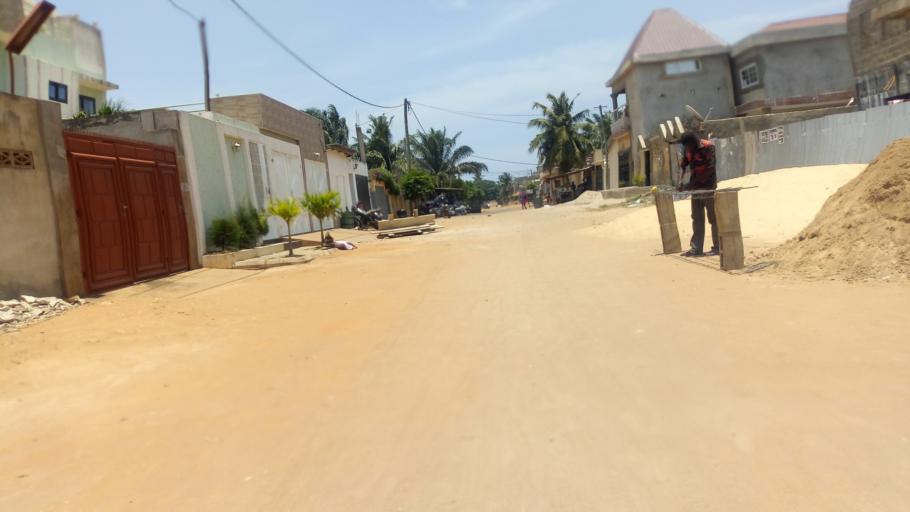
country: TG
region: Maritime
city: Lome
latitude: 6.1904
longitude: 1.1790
